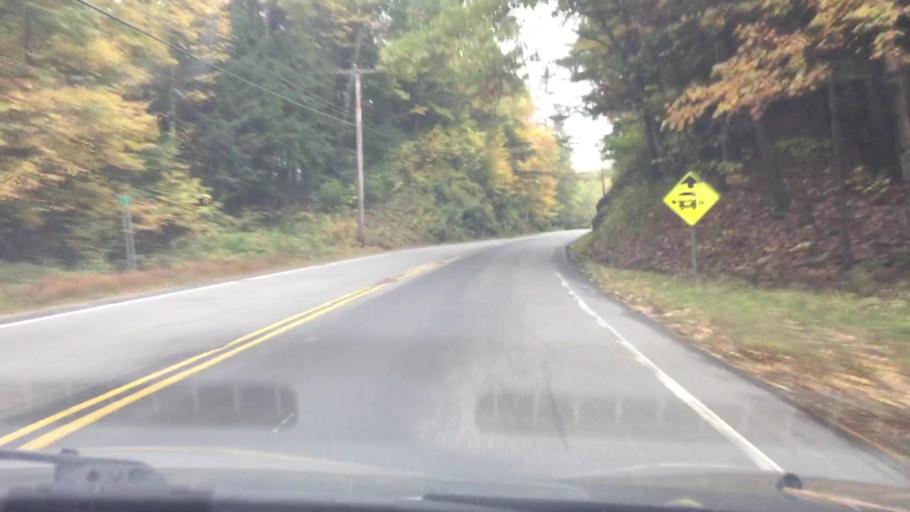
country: US
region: New Hampshire
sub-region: Cheshire County
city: Keene
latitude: 43.0314
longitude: -72.2686
